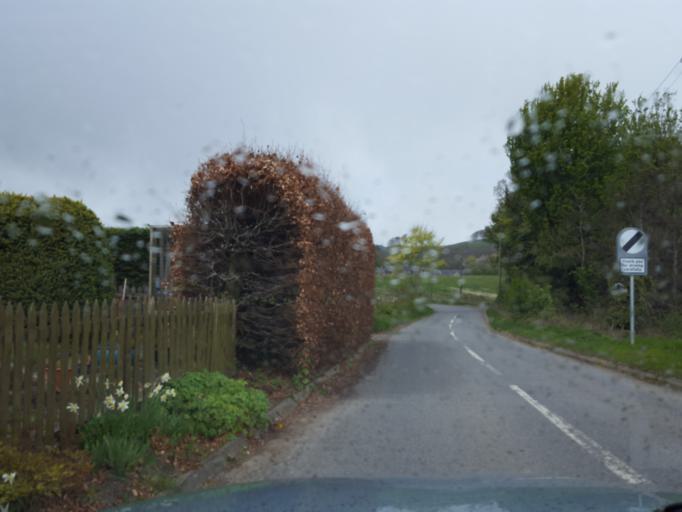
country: GB
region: Scotland
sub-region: Perth and Kinross
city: Errol
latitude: 56.4252
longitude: -3.2498
